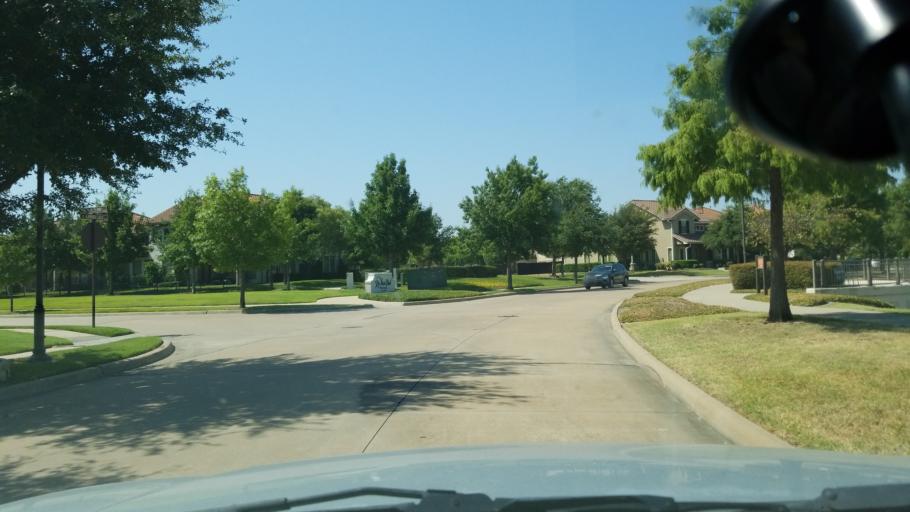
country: US
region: Texas
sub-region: Dallas County
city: Farmers Branch
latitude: 32.8990
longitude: -96.9311
